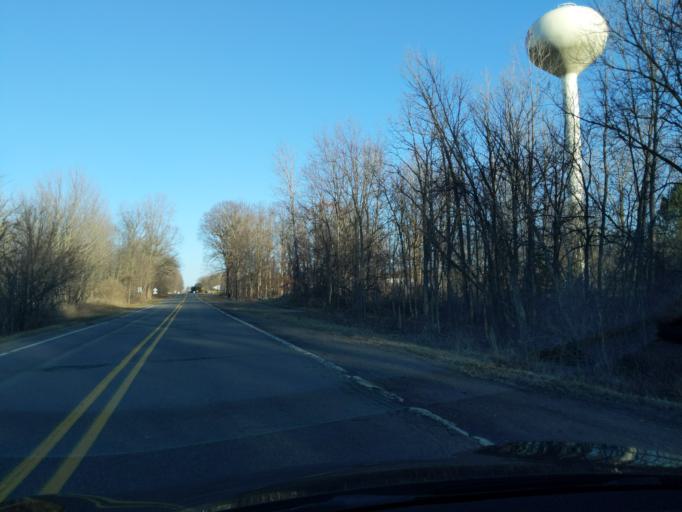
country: US
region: Michigan
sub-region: Ingham County
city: Mason
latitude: 42.5965
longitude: -84.4601
